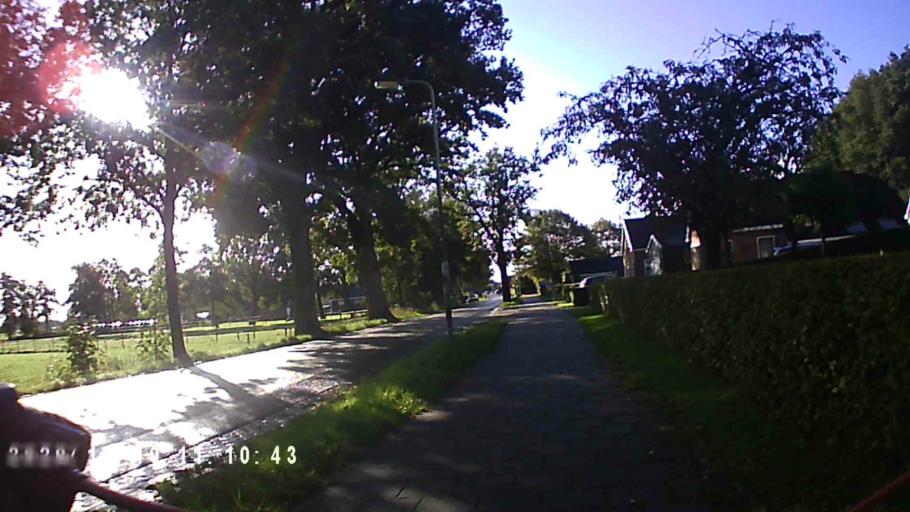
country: NL
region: Friesland
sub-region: Gemeente Smallingerland
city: Drachtstercompagnie
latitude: 53.1151
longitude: 6.2061
